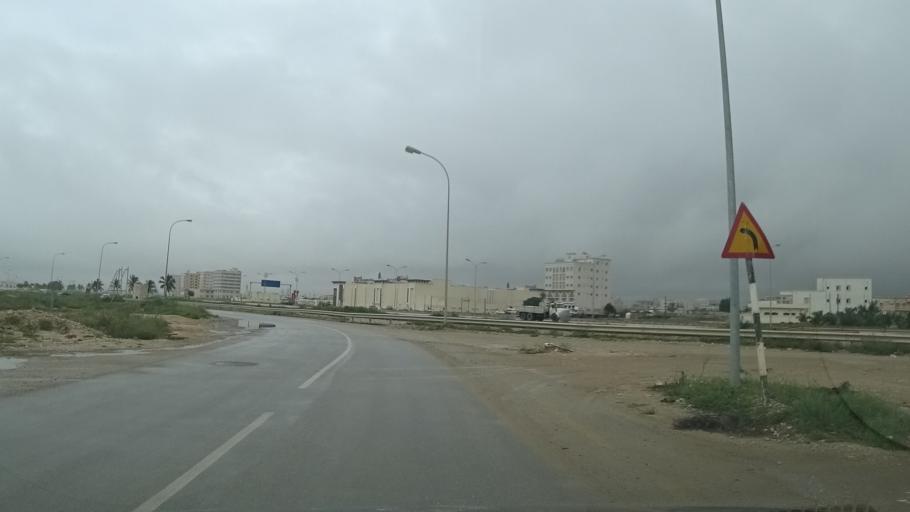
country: OM
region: Zufar
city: Salalah
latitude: 16.9987
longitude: 54.0353
